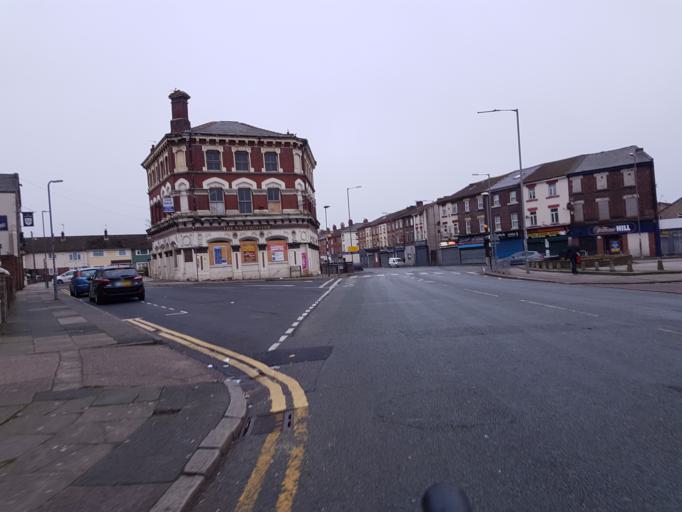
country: GB
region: England
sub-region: Liverpool
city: Liverpool
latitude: 53.4375
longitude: -2.9742
